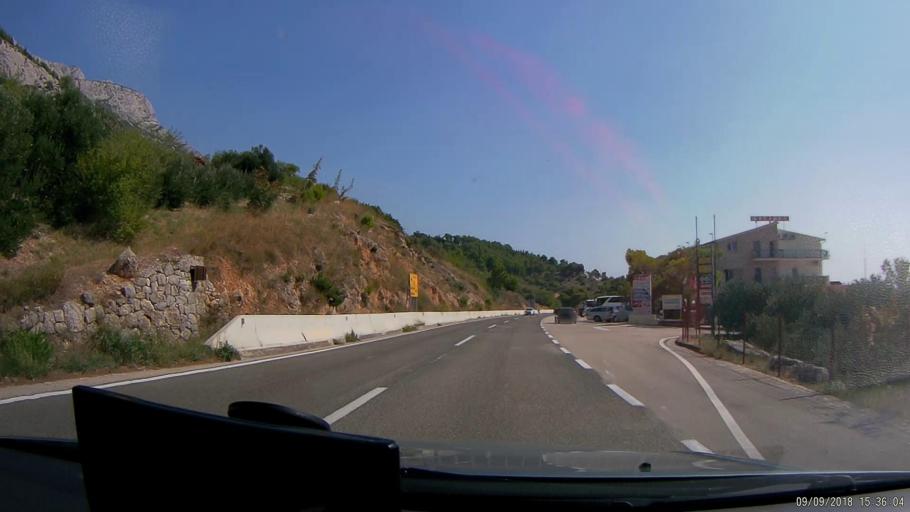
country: HR
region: Splitsko-Dalmatinska
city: Donja Brela
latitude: 43.3811
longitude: 16.9210
